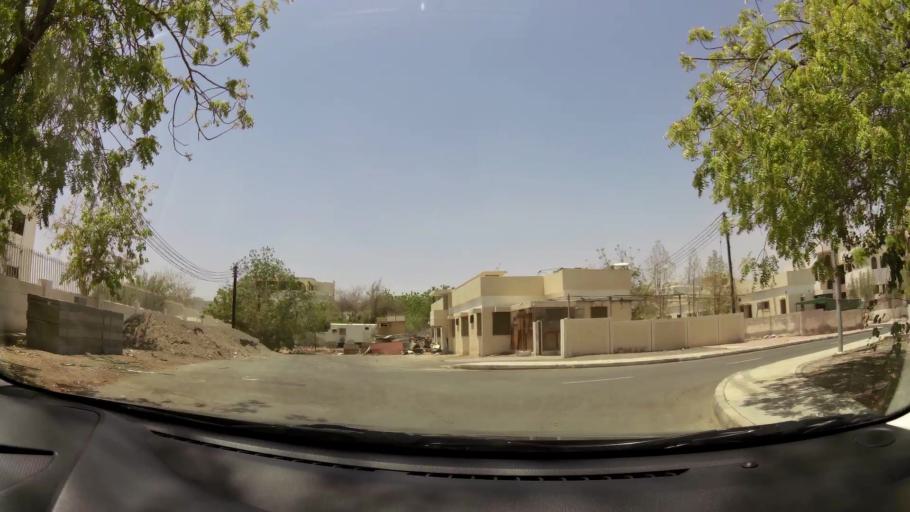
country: OM
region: Muhafazat Masqat
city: Bawshar
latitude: 23.6075
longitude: 58.4687
